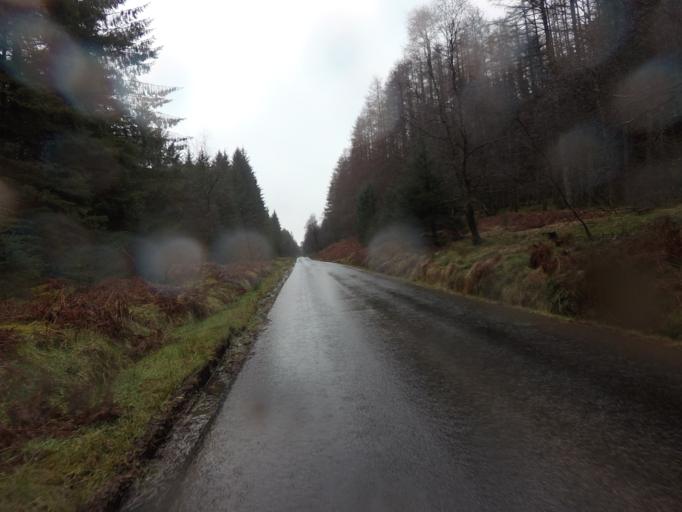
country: GB
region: Scotland
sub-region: West Dunbartonshire
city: Balloch
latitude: 56.2291
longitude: -4.5562
